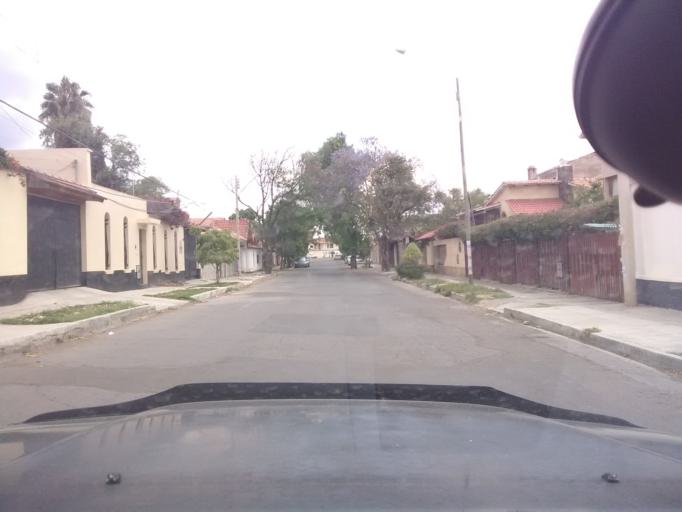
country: BO
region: Cochabamba
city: Cochabamba
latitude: -17.3647
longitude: -66.1734
